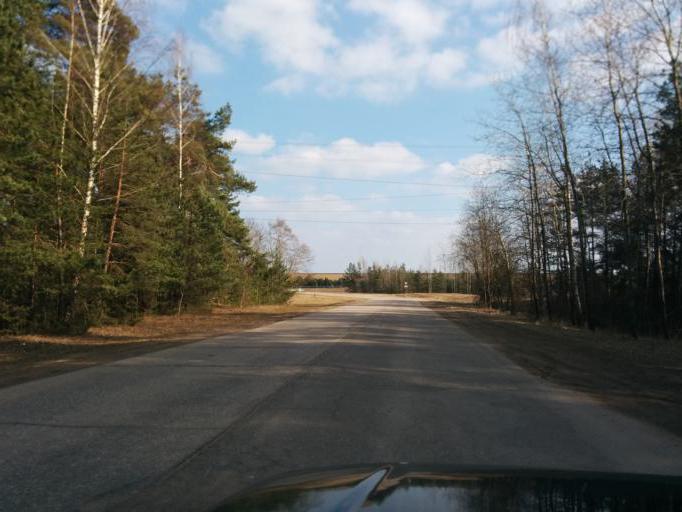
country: LV
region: Kekava
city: Kekava
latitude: 56.8498
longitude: 24.2640
